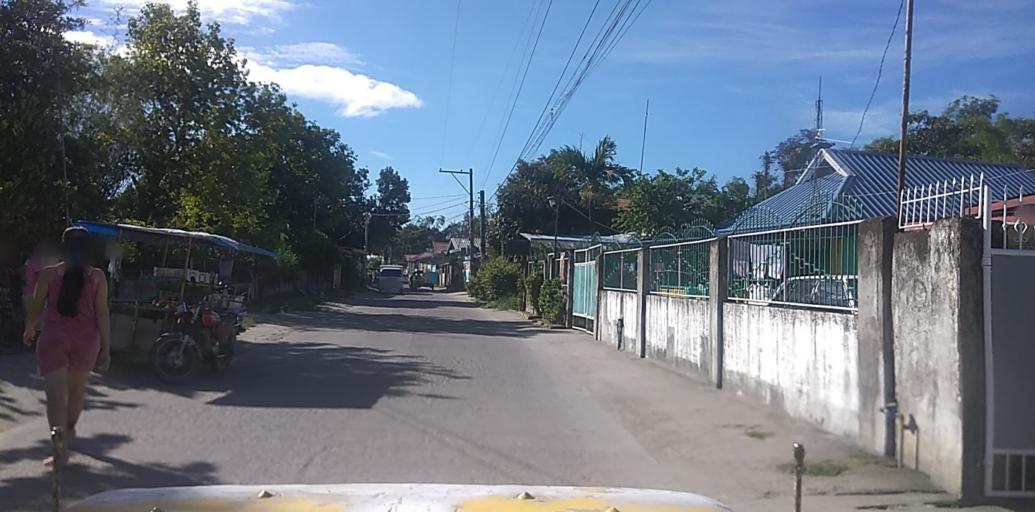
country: PH
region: Central Luzon
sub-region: Province of Pampanga
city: San Patricio
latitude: 15.1000
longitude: 120.7136
